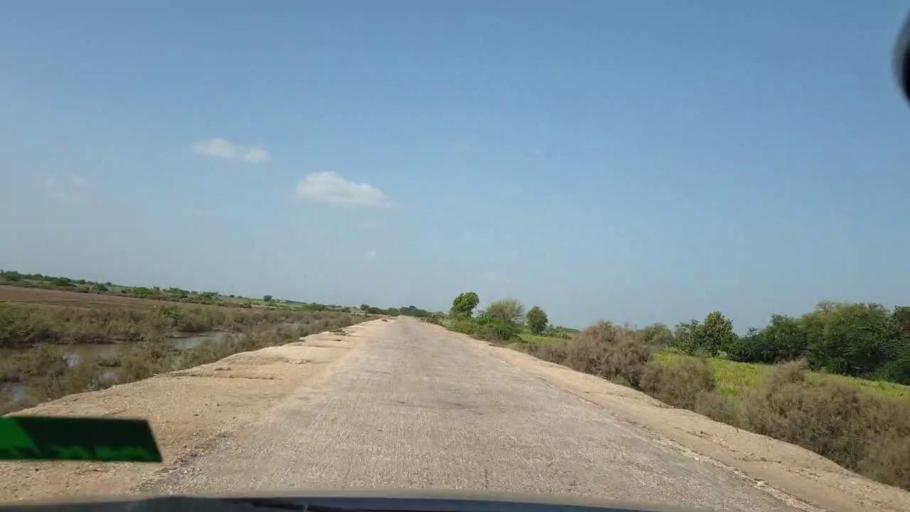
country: PK
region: Sindh
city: Tando Bago
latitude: 24.6920
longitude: 69.1891
